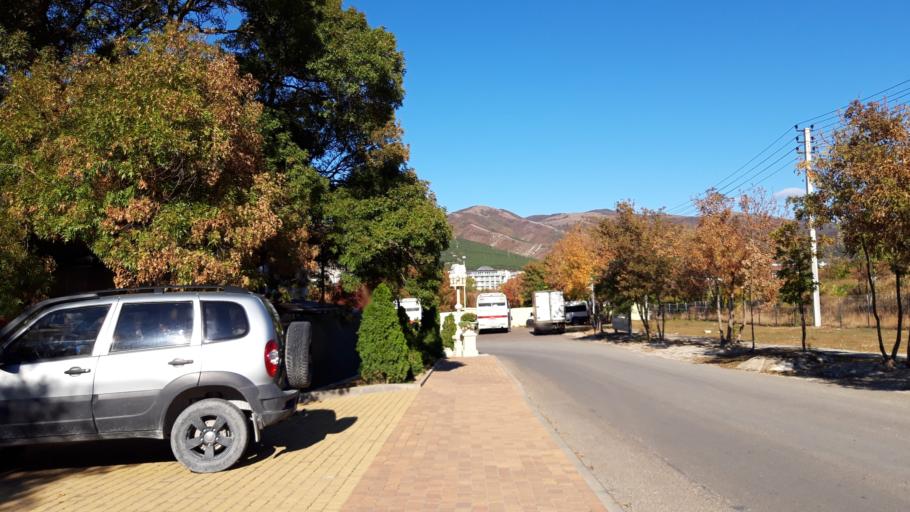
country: RU
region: Krasnodarskiy
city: Kabardinka
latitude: 44.6437
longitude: 37.9358
